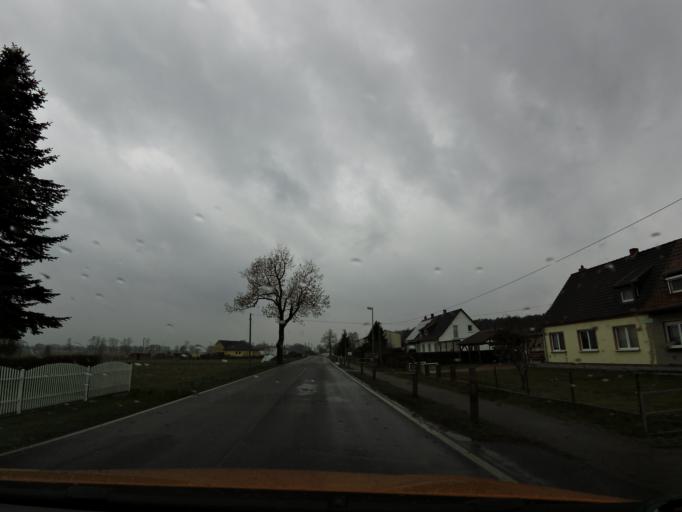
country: DE
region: Brandenburg
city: Ziesar
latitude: 52.3214
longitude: 12.3485
